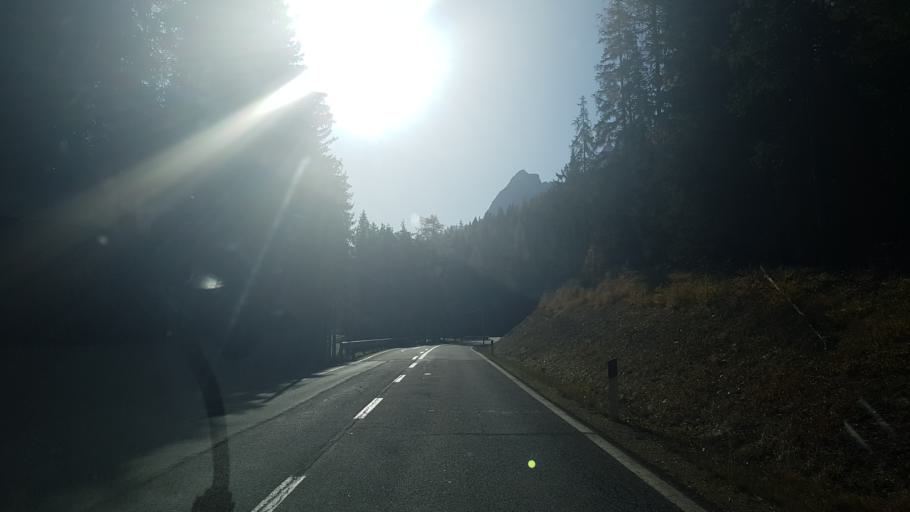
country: IT
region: Trentino-Alto Adige
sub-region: Bolzano
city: Sesto
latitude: 46.6745
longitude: 12.3868
